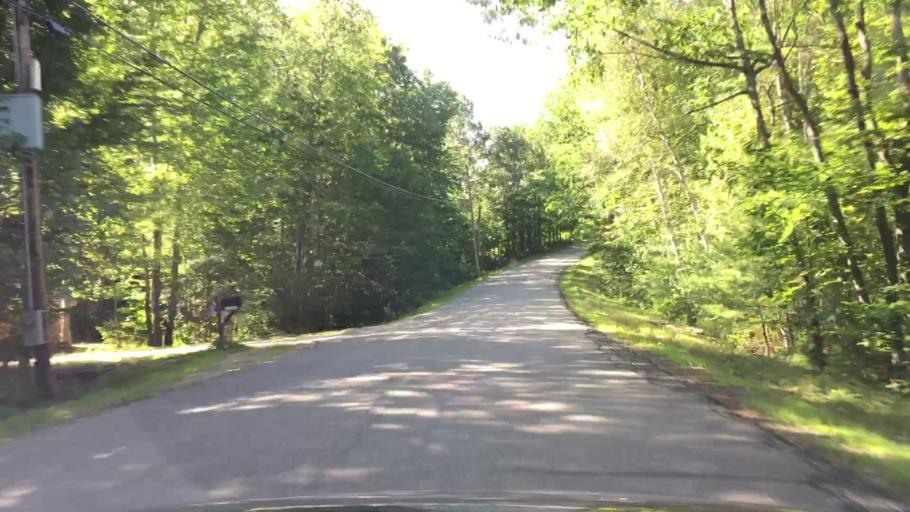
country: US
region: New Hampshire
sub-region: Grafton County
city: Ashland
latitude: 43.7186
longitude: -71.6299
